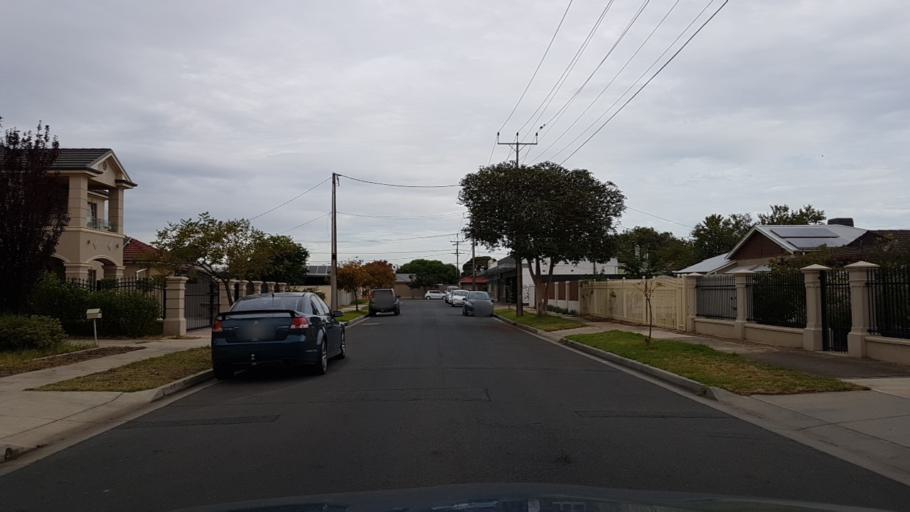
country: AU
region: South Australia
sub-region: Charles Sturt
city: Woodville North
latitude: -34.8608
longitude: 138.5425
